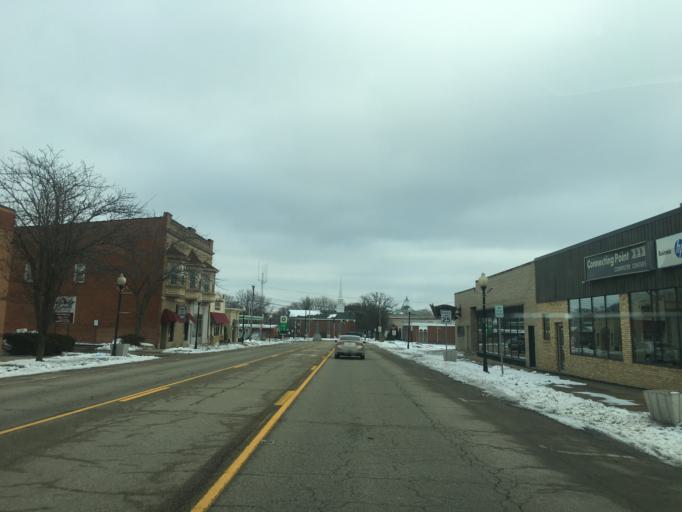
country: US
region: Illinois
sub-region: LaSalle County
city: Peru
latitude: 41.3276
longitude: -89.1278
